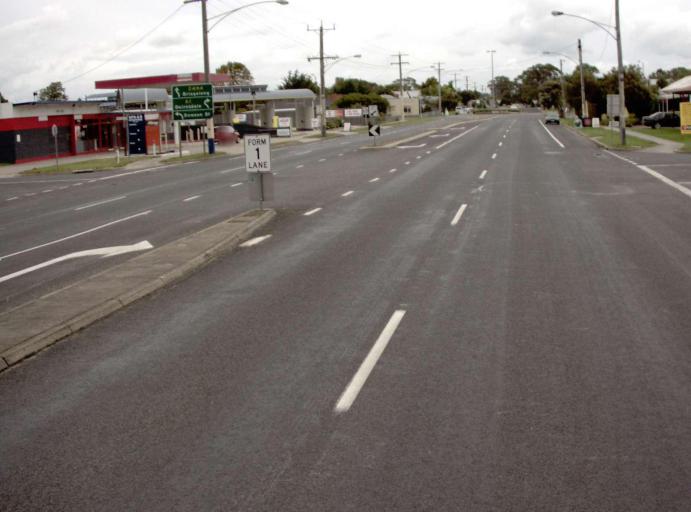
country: AU
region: Victoria
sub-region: Wellington
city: Sale
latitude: -37.9652
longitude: 147.0802
